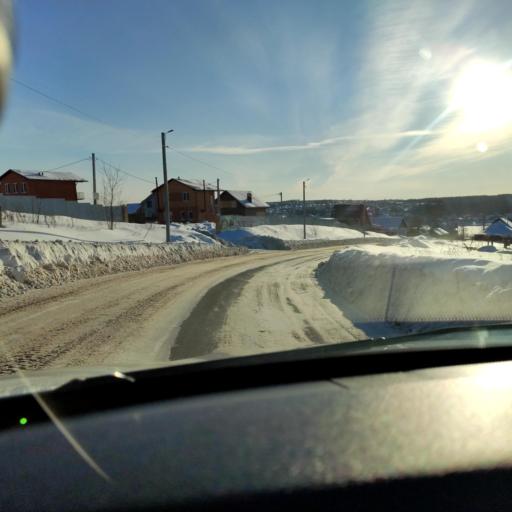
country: RU
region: Perm
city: Polazna
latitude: 58.3116
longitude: 56.4286
